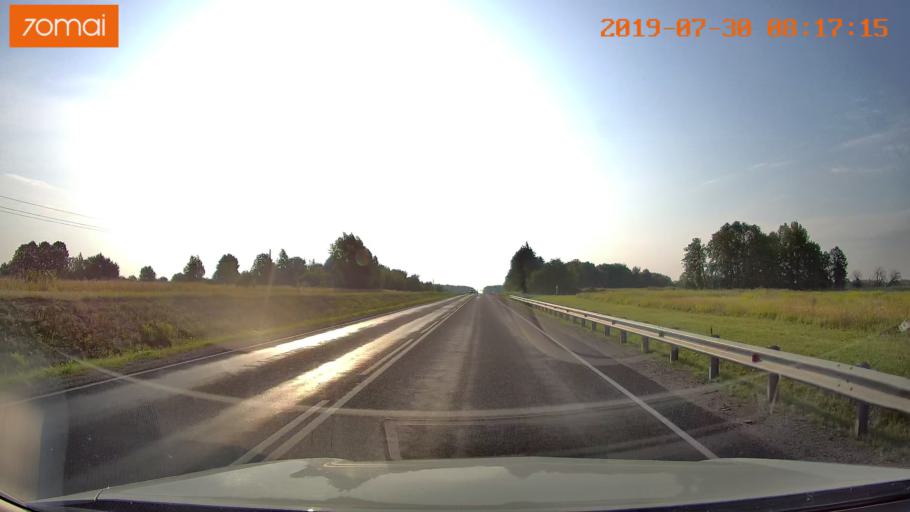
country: RU
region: Kaliningrad
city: Zheleznodorozhnyy
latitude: 54.6371
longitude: 21.4324
